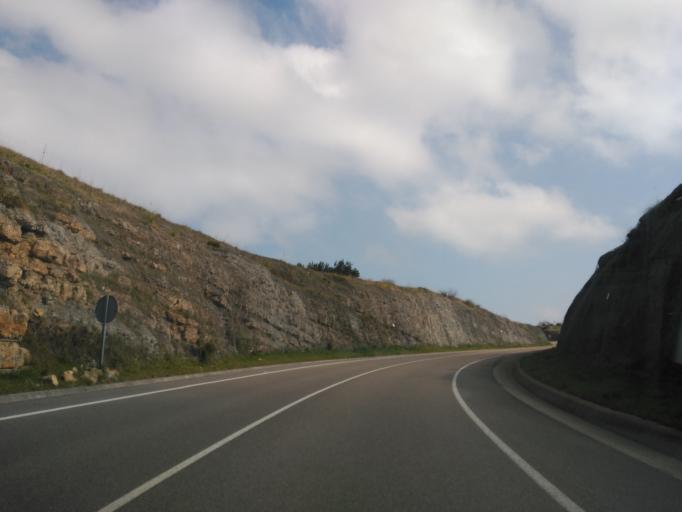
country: ES
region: Cantabria
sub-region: Provincia de Cantabria
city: Santillana
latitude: 43.3837
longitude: -4.1002
